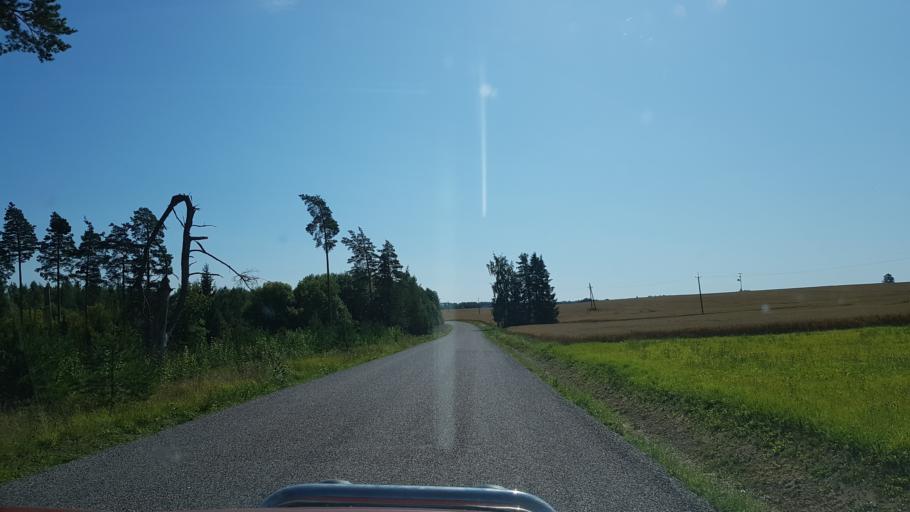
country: EE
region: Tartu
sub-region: Puhja vald
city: Puhja
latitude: 58.2519
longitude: 26.3324
